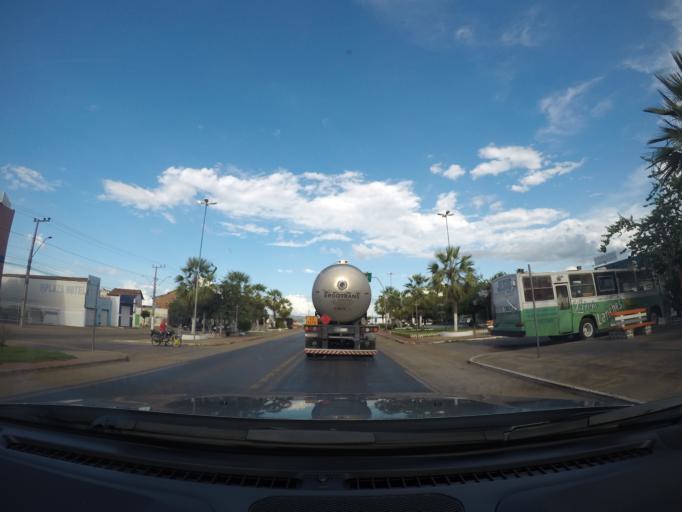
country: BR
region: Bahia
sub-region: Ibotirama
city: Ibotirama
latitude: -12.1781
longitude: -43.2192
